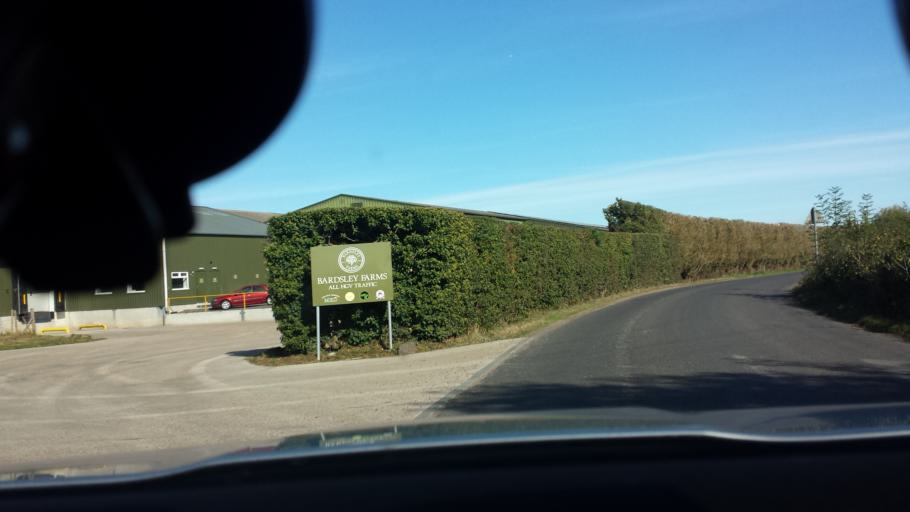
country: GB
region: England
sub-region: Kent
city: Staplehurst
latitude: 51.1929
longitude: 0.5497
